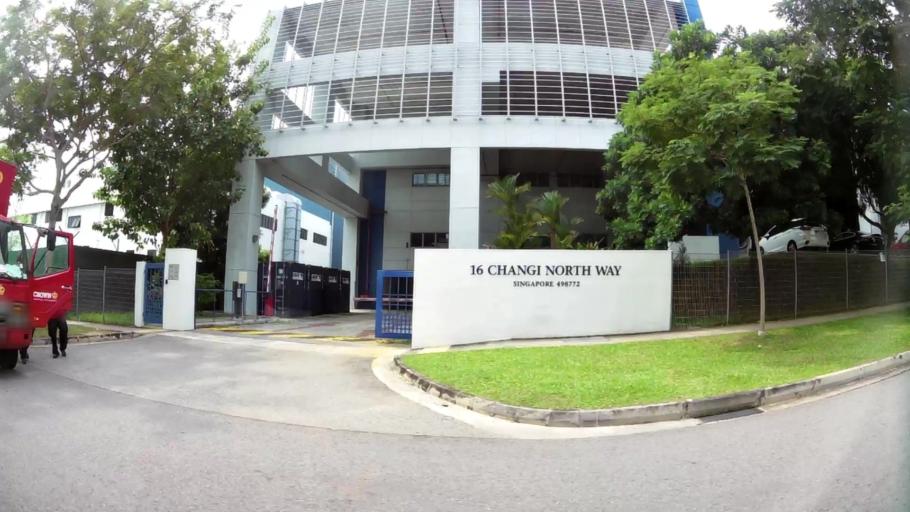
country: SG
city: Singapore
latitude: 1.3524
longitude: 103.9730
